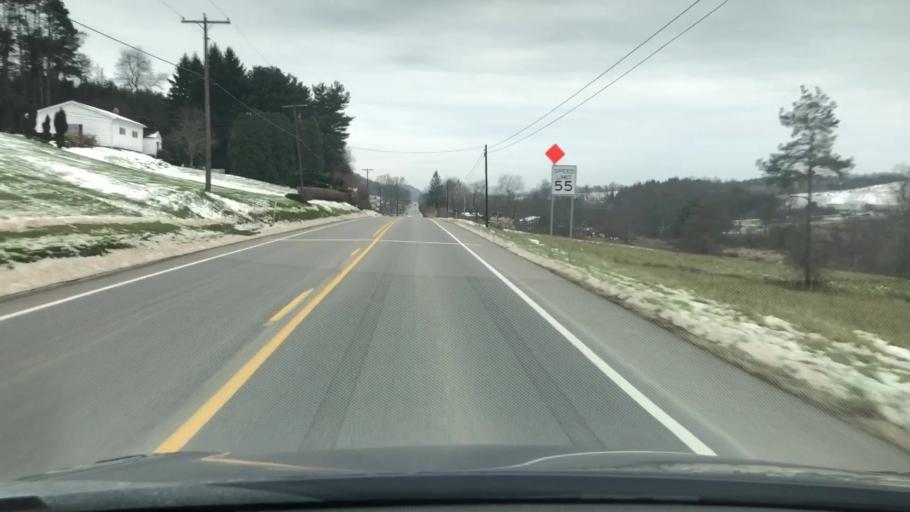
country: US
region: Pennsylvania
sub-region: Jefferson County
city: Brookville
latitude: 41.0867
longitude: -79.2294
